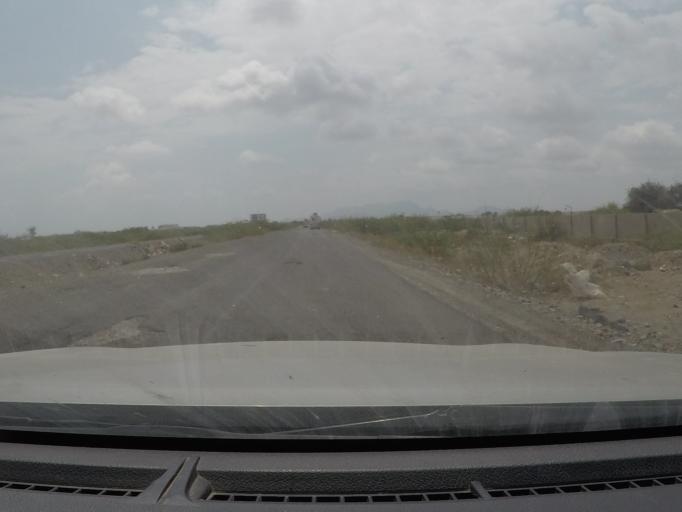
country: YE
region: Aden
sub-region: Ash Shaikh Outhman
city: Ash Shaykh `Uthman
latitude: 12.9114
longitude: 45.0097
